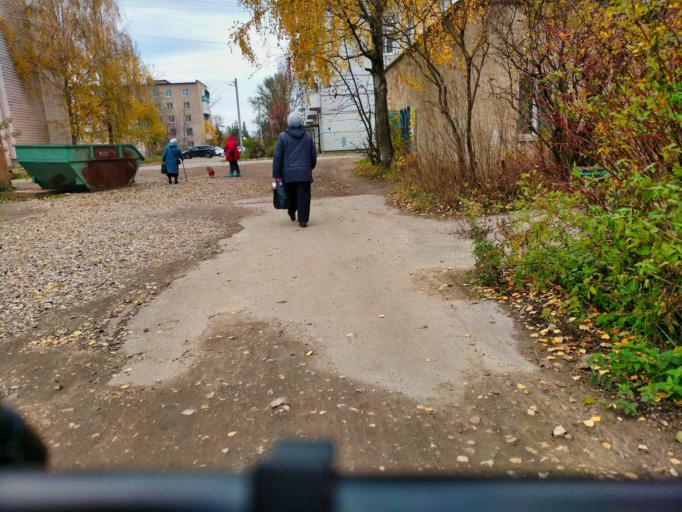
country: RU
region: Tverskaya
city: Rzhev
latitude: 56.2475
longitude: 34.3338
